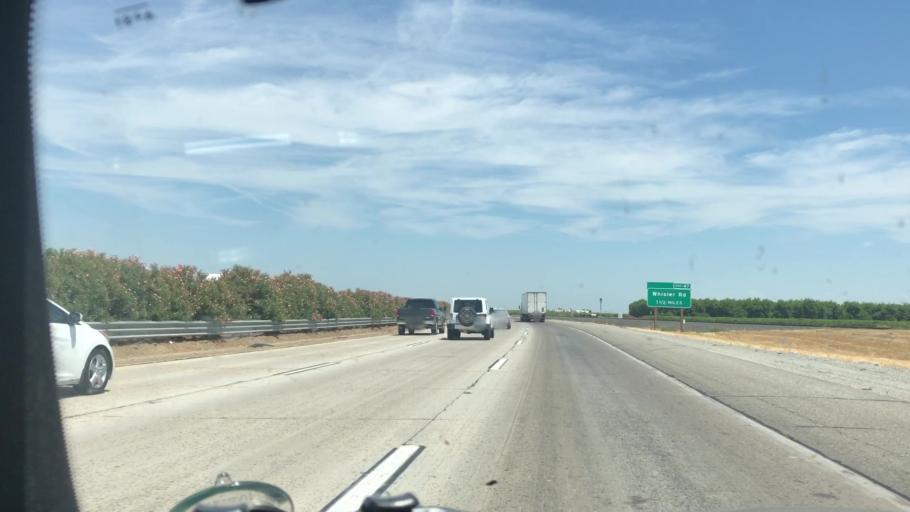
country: US
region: California
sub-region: Kern County
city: McFarland
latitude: 35.6126
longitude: -119.2119
